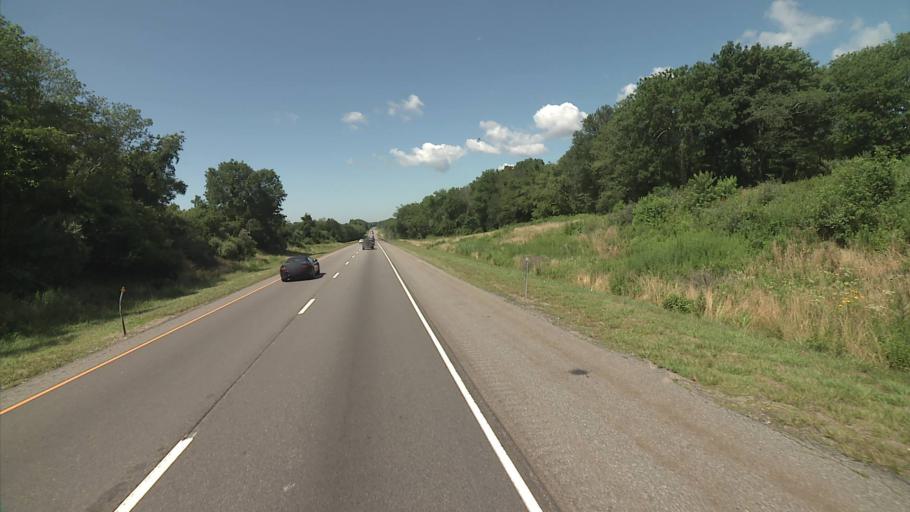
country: US
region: Connecticut
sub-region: New London County
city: Pawcatuck
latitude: 41.3849
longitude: -71.8913
